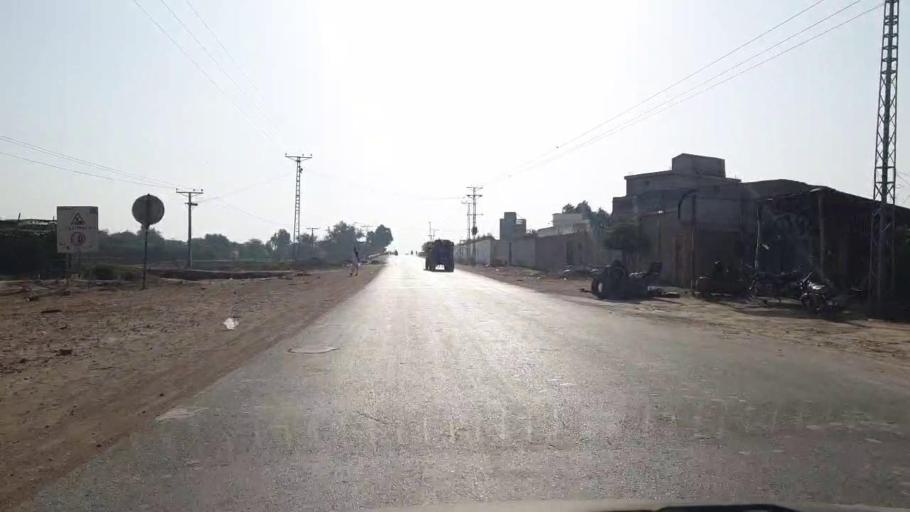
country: PK
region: Sindh
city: Badin
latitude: 24.6763
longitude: 68.8487
